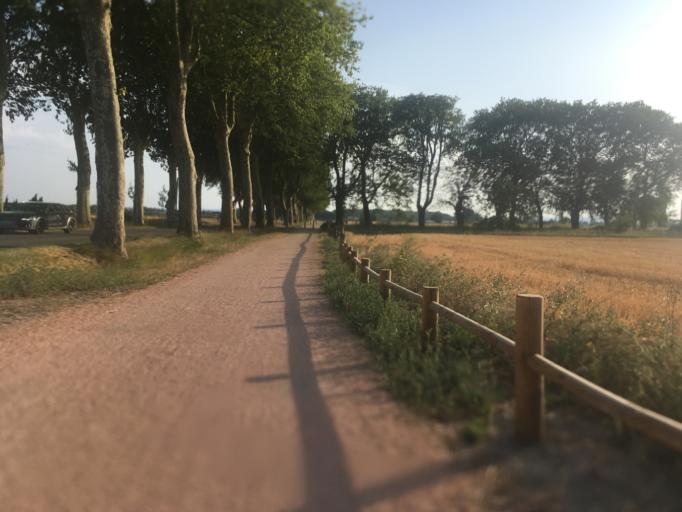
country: FR
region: Languedoc-Roussillon
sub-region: Departement de l'Aude
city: Bram
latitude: 43.2530
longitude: 2.1251
